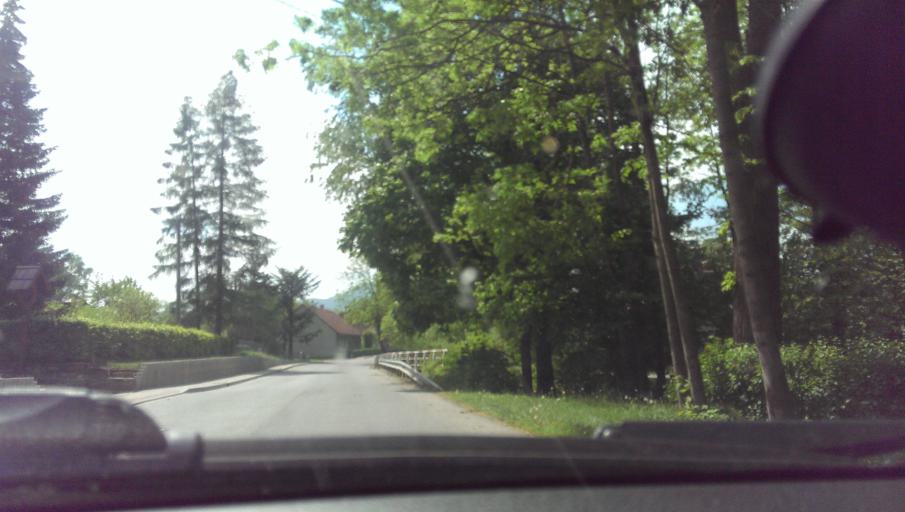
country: CZ
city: Lichnov (o. Novy Jicin)
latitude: 49.5736
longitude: 18.1812
